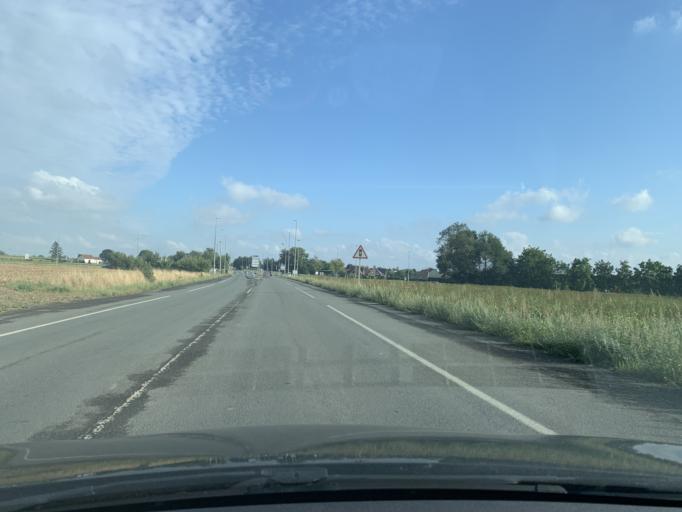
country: FR
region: Nord-Pas-de-Calais
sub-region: Departement du Nord
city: Emmerin
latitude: 50.6002
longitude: 3.0017
